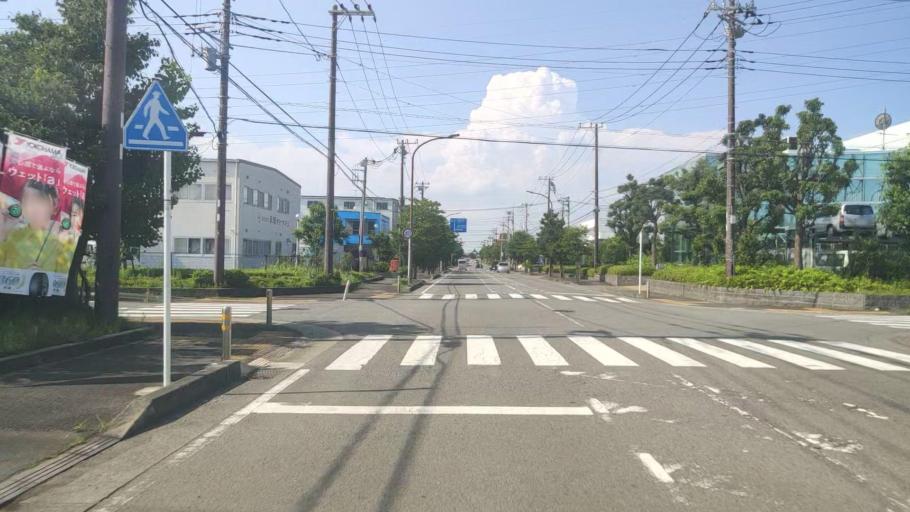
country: JP
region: Kanagawa
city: Hiratsuka
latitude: 35.3579
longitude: 139.3398
